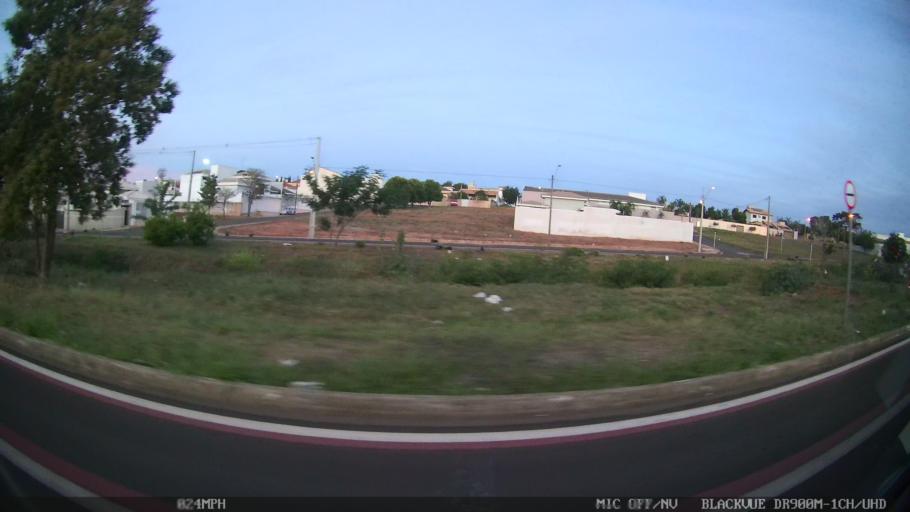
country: BR
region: Sao Paulo
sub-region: Catanduva
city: Catanduva
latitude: -21.1481
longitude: -48.9927
